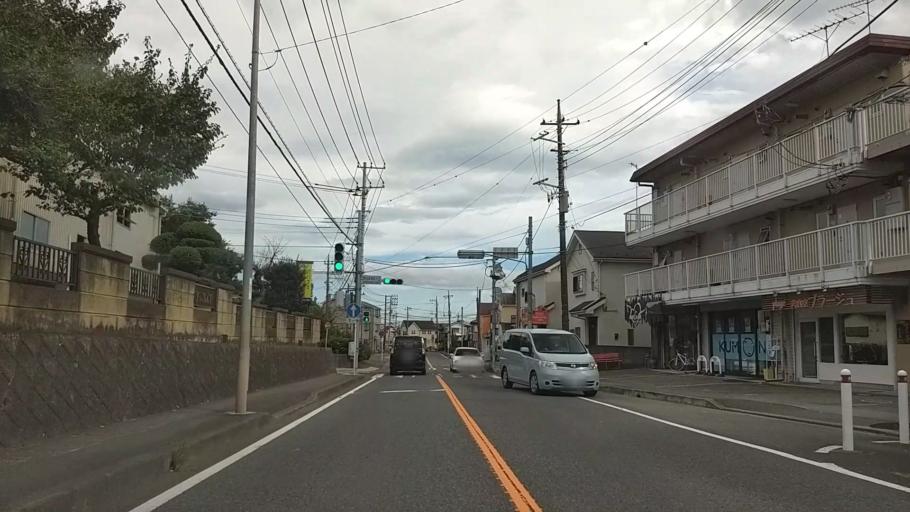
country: JP
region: Tokyo
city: Hachioji
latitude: 35.5868
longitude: 139.3174
